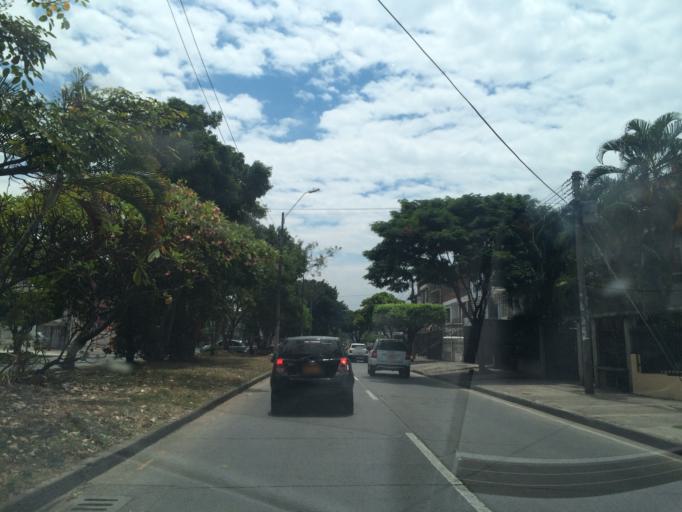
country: CO
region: Valle del Cauca
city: Cali
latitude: 3.4085
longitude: -76.5263
